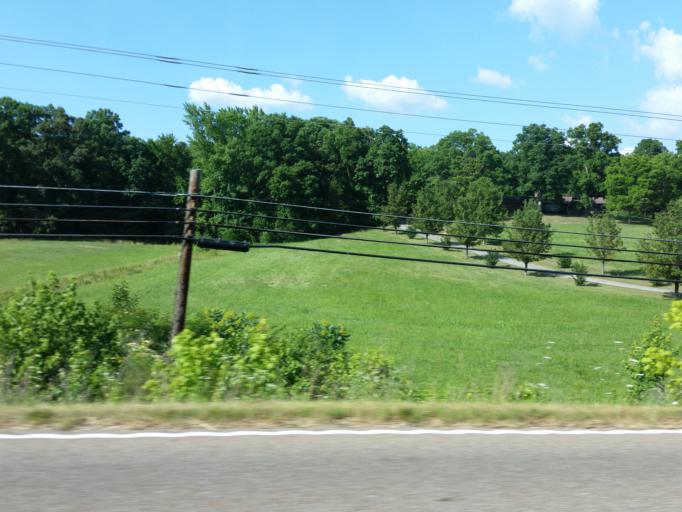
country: US
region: Tennessee
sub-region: Decatur County
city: Parsons
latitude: 35.6480
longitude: -88.1113
